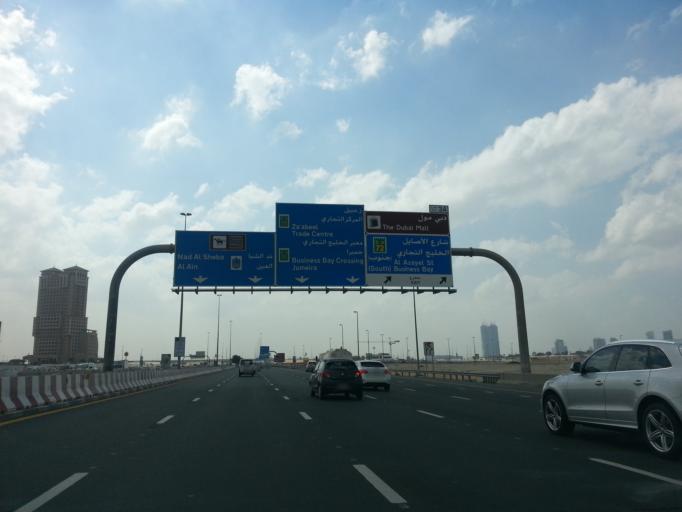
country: AE
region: Ash Shariqah
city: Sharjah
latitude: 25.2183
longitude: 55.3145
